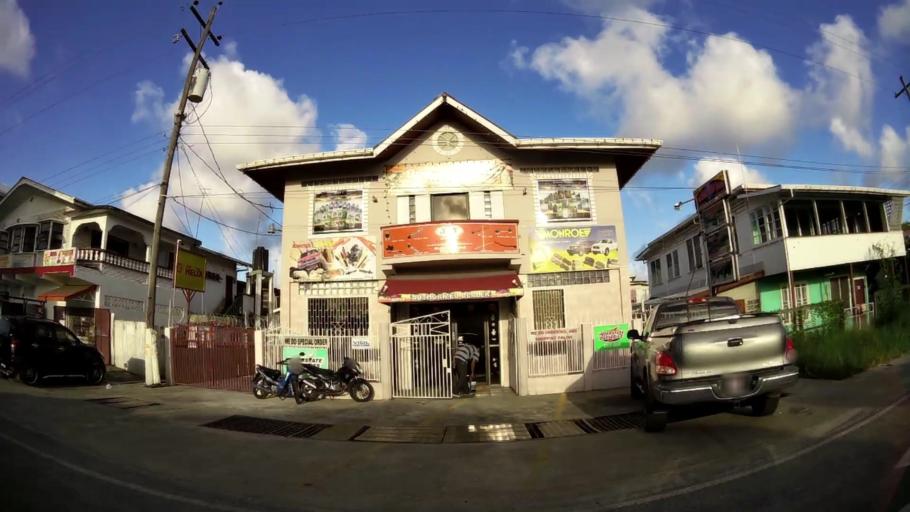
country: GY
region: Demerara-Mahaica
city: Georgetown
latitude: 6.8095
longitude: -58.1375
